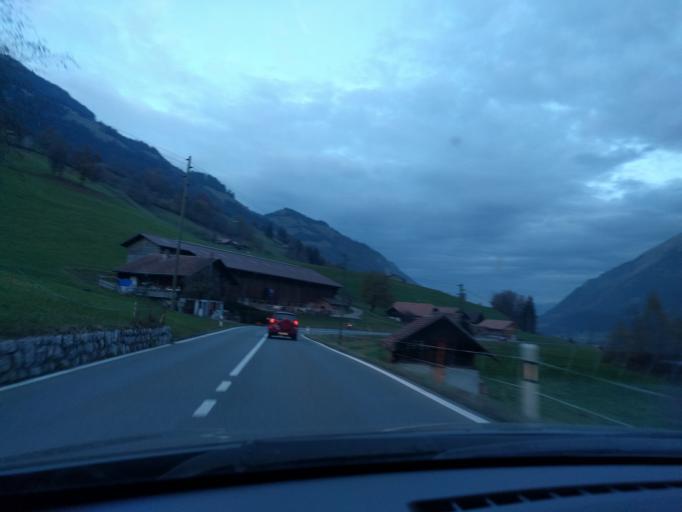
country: CH
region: Bern
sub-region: Frutigen-Niedersimmental District
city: Erlenbach im Simmental
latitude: 46.6596
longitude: 7.5361
